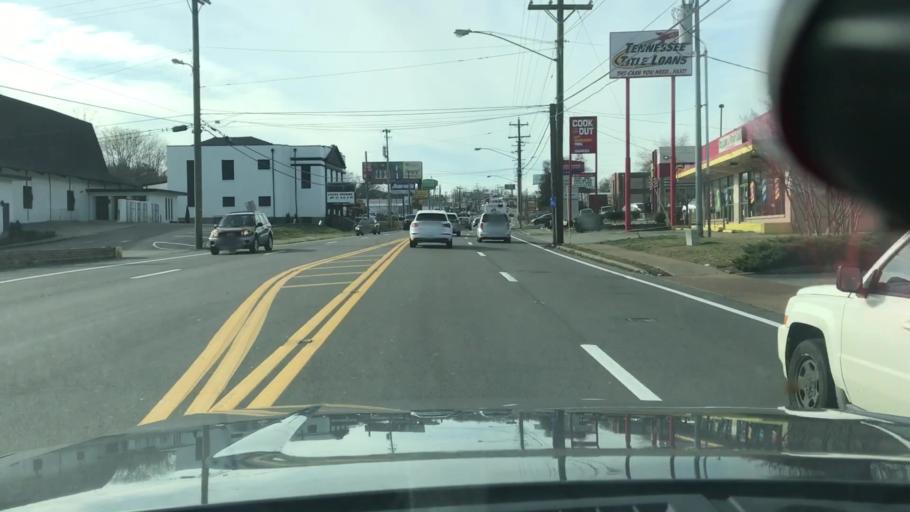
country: US
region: Tennessee
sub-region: Davidson County
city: Belle Meade
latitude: 36.1495
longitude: -86.8608
